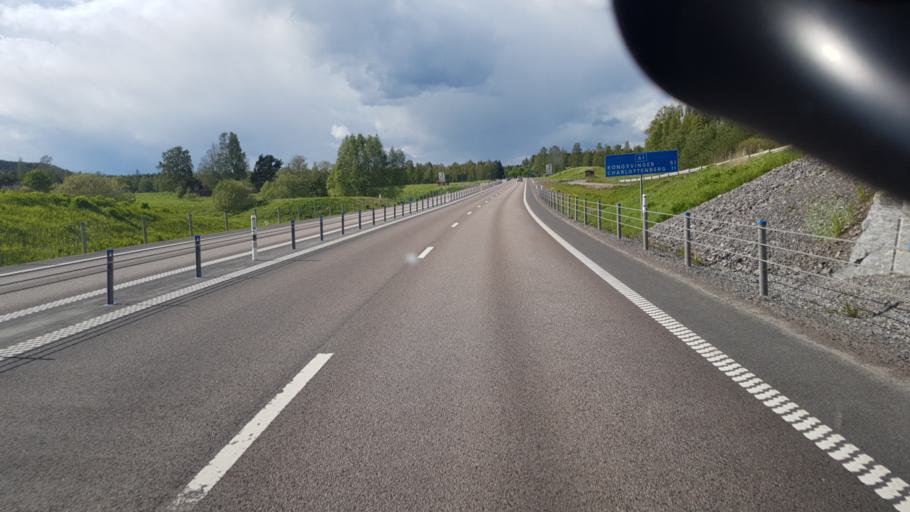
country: SE
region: Vaermland
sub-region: Eda Kommun
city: Amotfors
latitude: 59.7889
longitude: 12.3439
